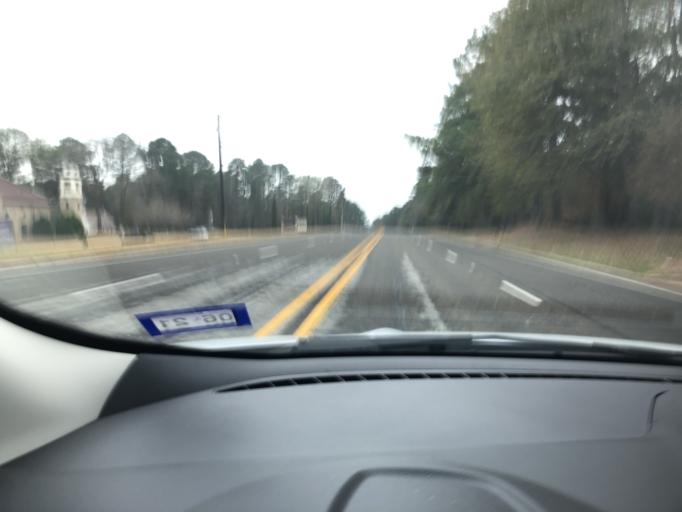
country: US
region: Texas
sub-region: Nacogdoches County
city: Nacogdoches
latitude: 31.6266
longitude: -94.6311
